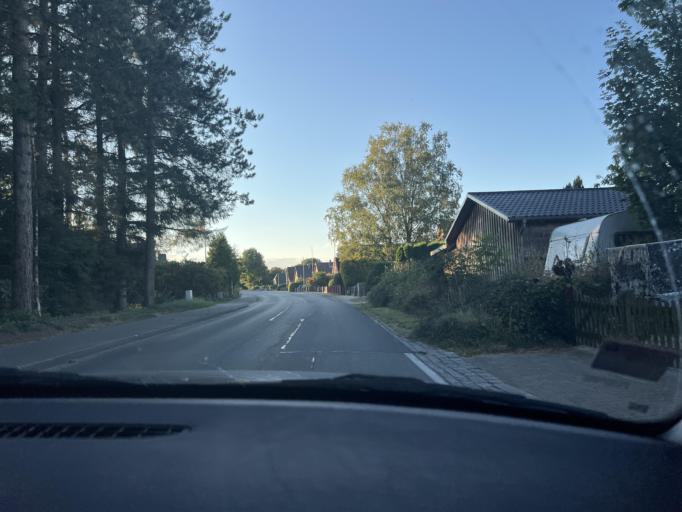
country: DE
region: Schleswig-Holstein
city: Suderheistedt
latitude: 54.2215
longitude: 9.1219
